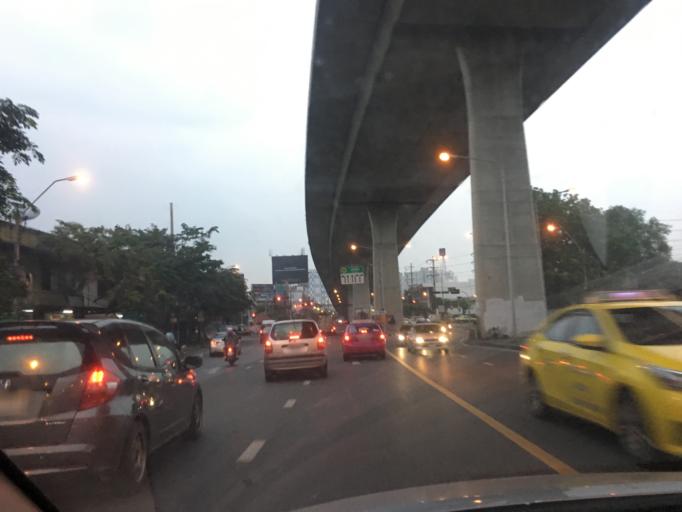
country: TH
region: Bangkok
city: Bang Kho Laem
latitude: 13.7024
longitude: 100.4894
